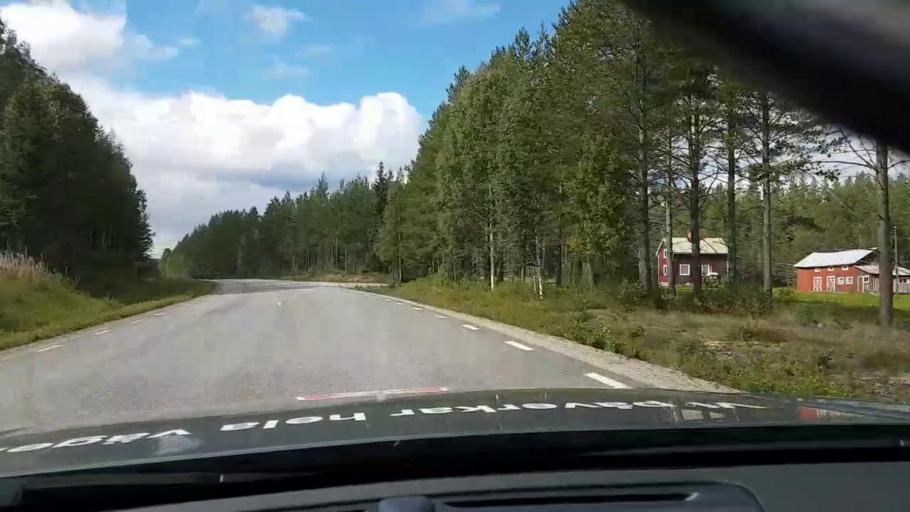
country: SE
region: Vaesternorrland
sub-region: OErnskoeldsviks Kommun
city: Bredbyn
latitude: 63.5301
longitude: 17.9836
